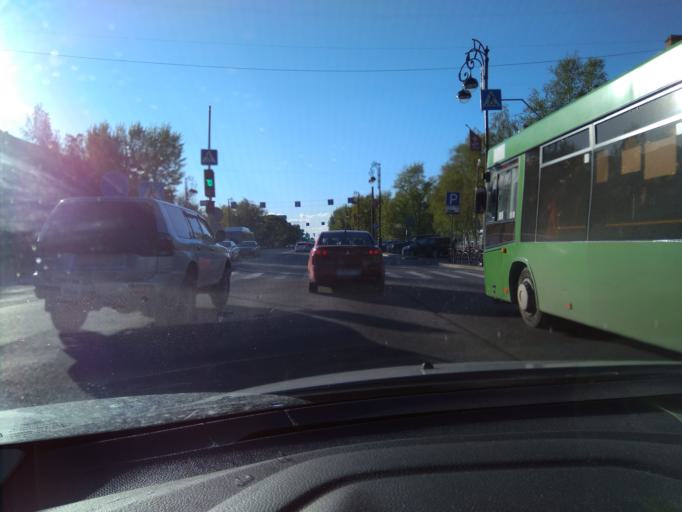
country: RU
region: Tjumen
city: Tyumen
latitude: 57.1343
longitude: 65.5768
